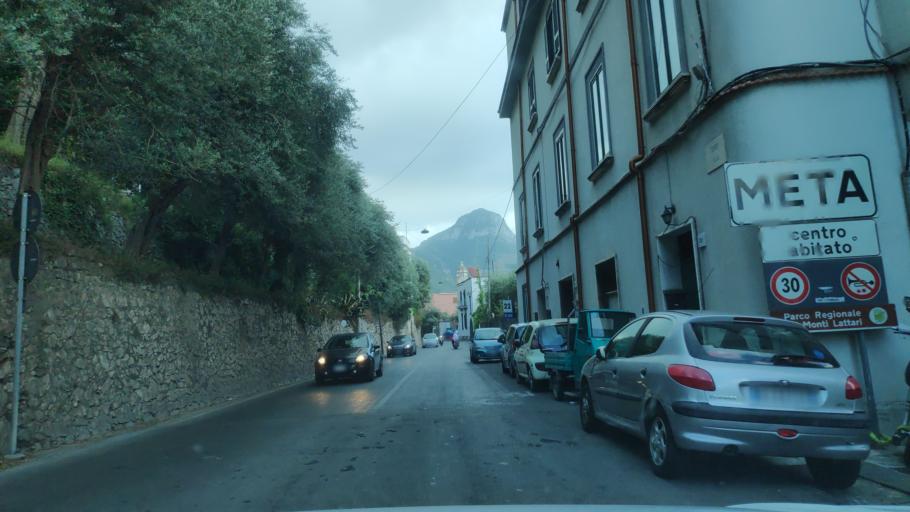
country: IT
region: Campania
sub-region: Provincia di Napoli
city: Meta
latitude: 40.6446
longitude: 14.4153
